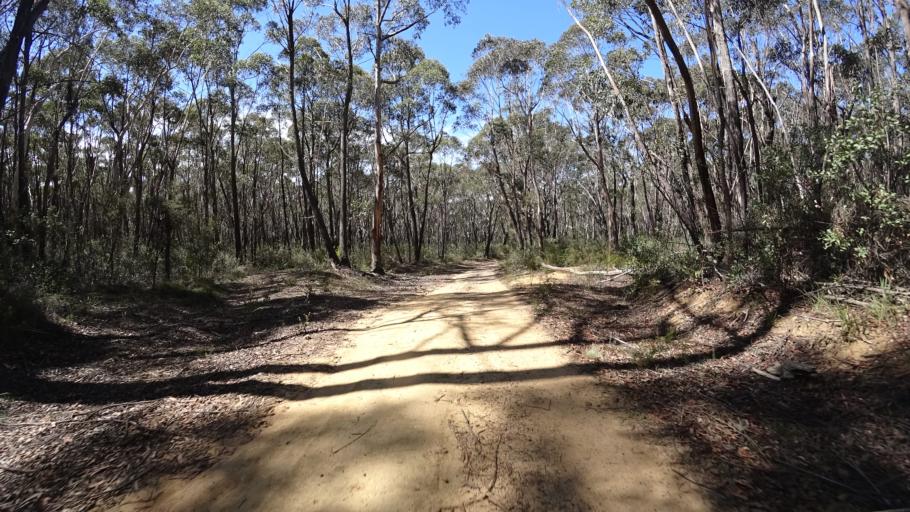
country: AU
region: New South Wales
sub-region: Lithgow
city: Lithgow
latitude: -33.3355
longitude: 150.2847
